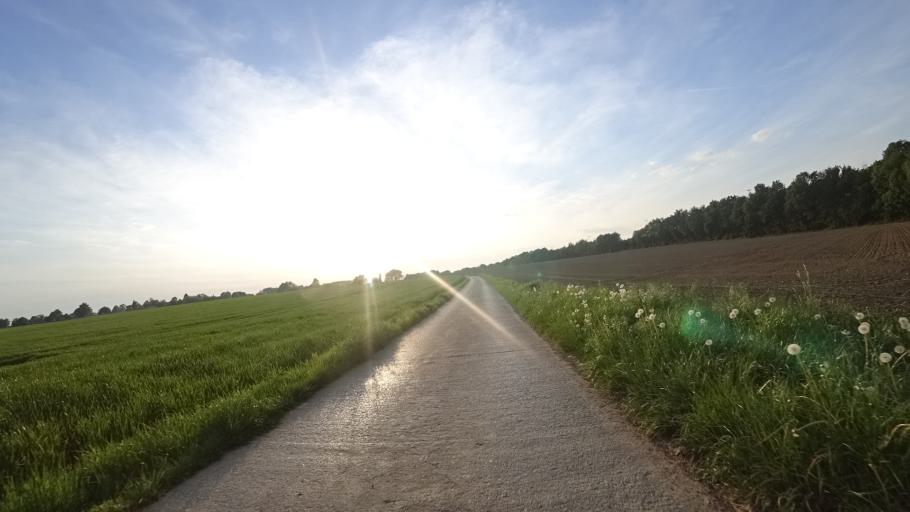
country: BE
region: Wallonia
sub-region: Province du Brabant Wallon
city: Walhain-Saint-Paul
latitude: 50.6452
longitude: 4.7196
